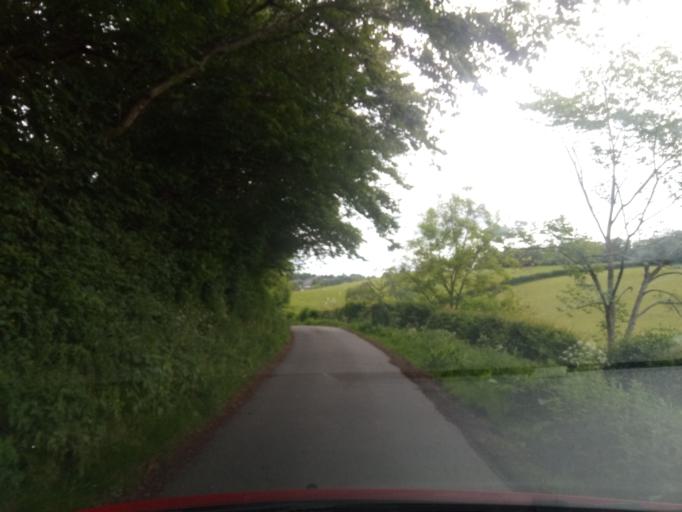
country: GB
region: Scotland
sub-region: The Scottish Borders
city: Selkirk
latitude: 55.5617
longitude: -2.8268
